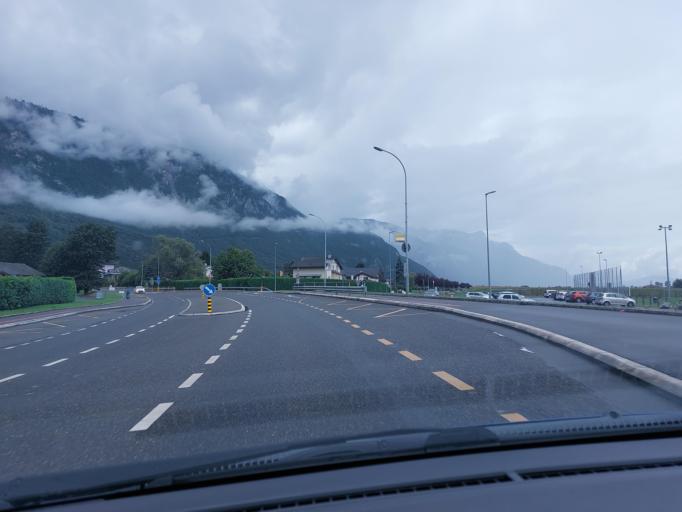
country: CH
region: Valais
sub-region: Monthey District
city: Collombey
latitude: 46.2779
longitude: 6.9368
